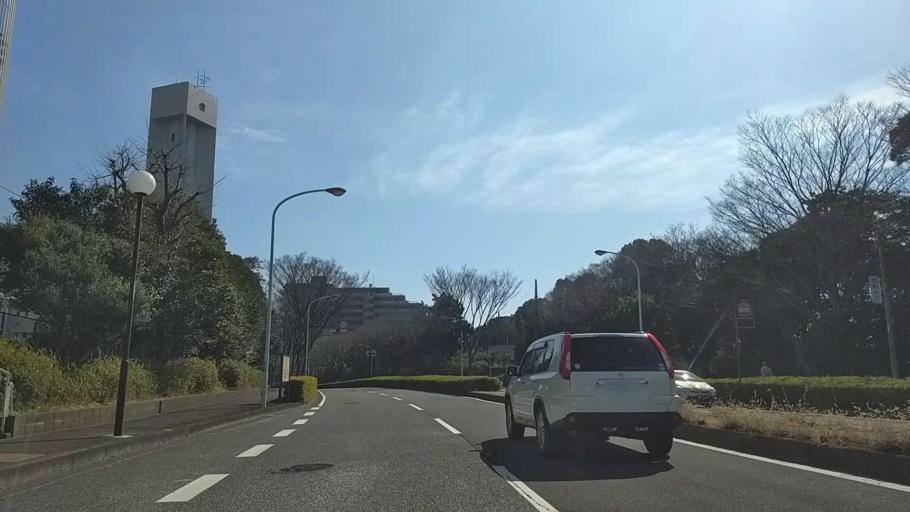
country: JP
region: Kanagawa
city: Fujisawa
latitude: 35.3559
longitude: 139.4427
